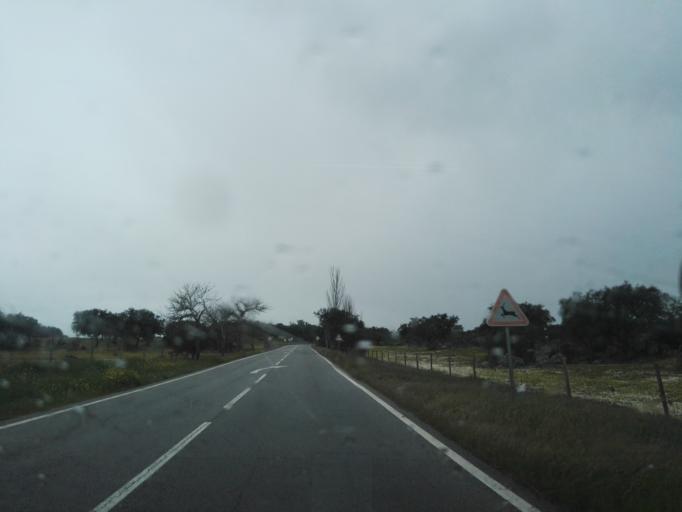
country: PT
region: Portalegre
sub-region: Arronches
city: Arronches
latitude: 39.0574
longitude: -7.2714
